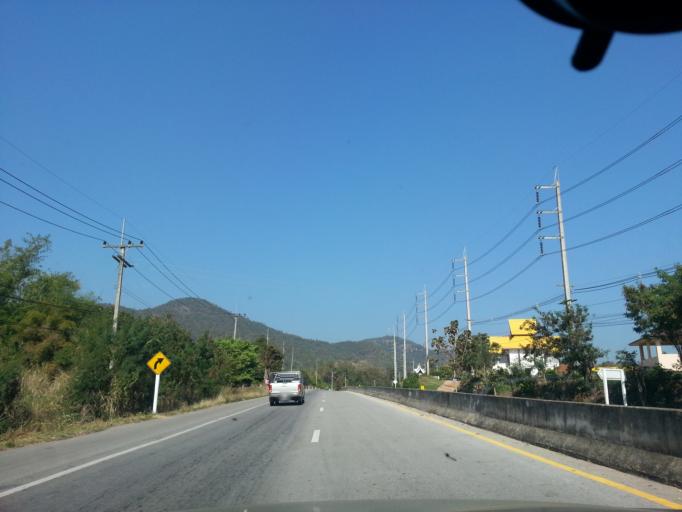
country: TH
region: Chiang Mai
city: Mae Taeng
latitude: 19.2226
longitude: 98.9718
